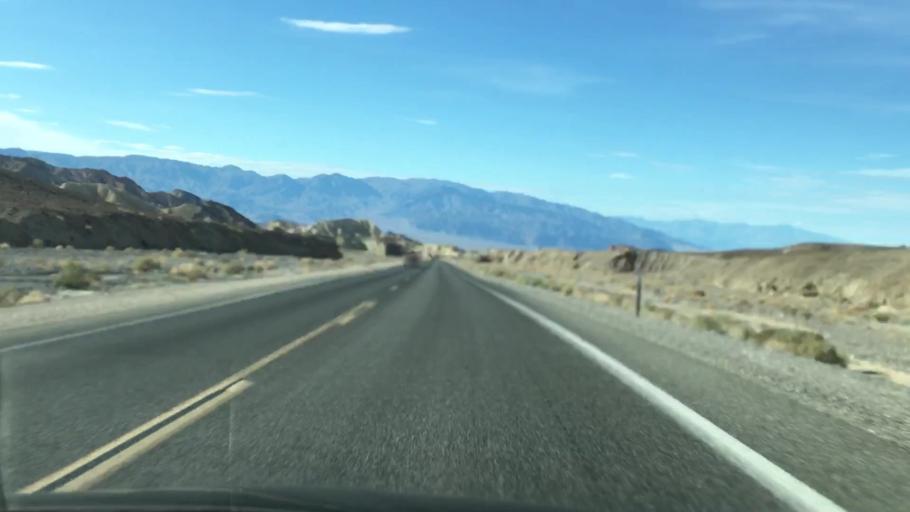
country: US
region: Nevada
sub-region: Nye County
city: Beatty
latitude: 36.4009
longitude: -116.7779
